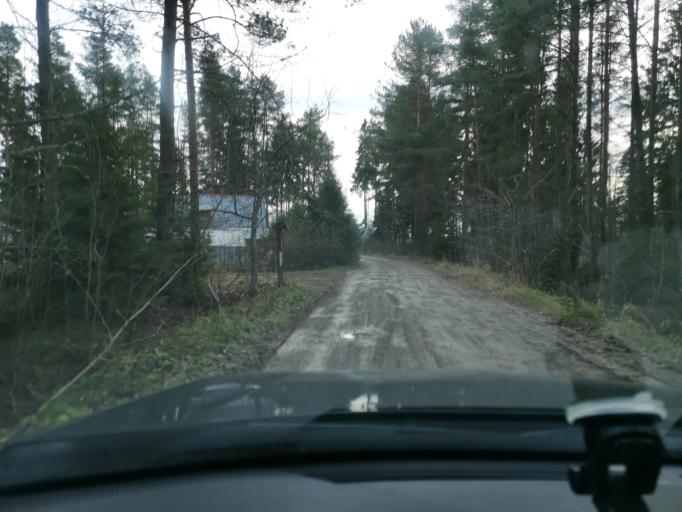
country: EE
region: Ida-Virumaa
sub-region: Sillamaee linn
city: Sillamae
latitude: 59.2544
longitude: 27.9136
